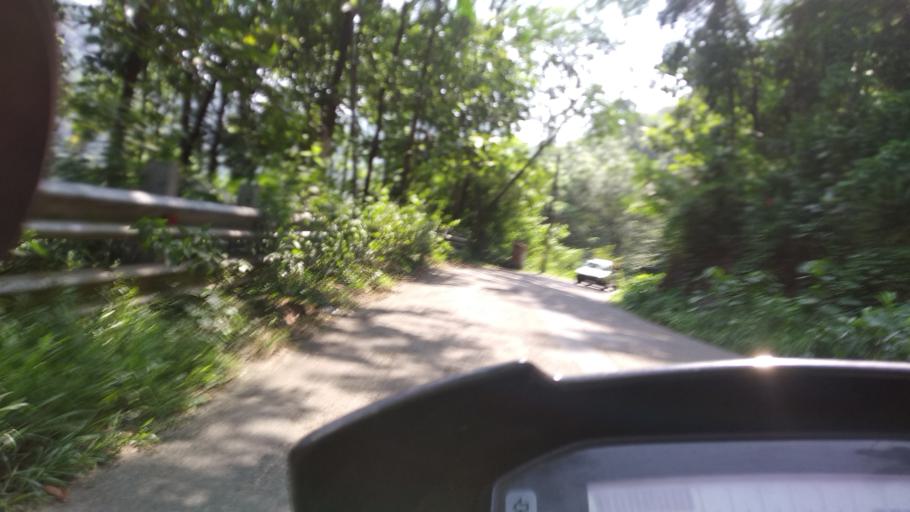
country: IN
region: Kerala
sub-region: Kottayam
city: Erattupetta
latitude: 9.6895
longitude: 76.8368
